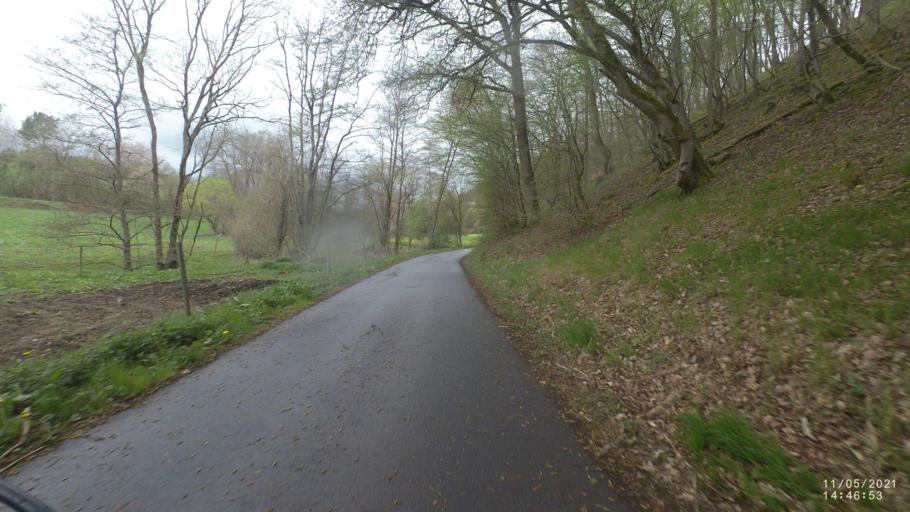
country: DE
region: Rheinland-Pfalz
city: Bermel
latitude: 50.2965
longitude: 7.0798
